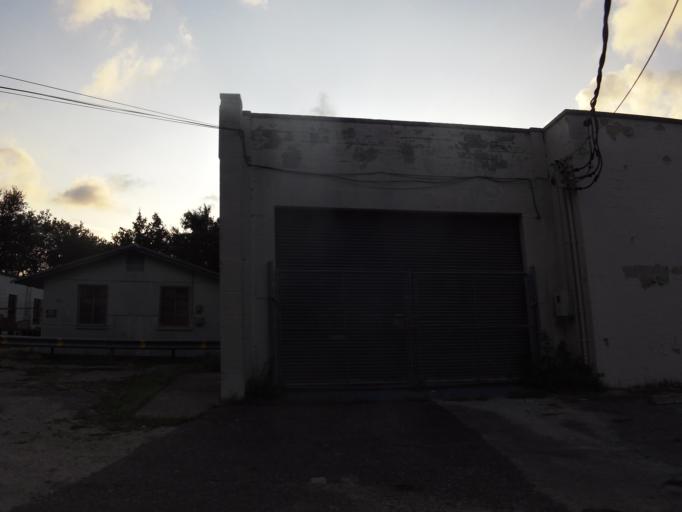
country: US
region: Florida
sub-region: Duval County
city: Jacksonville
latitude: 30.3234
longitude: -81.6869
